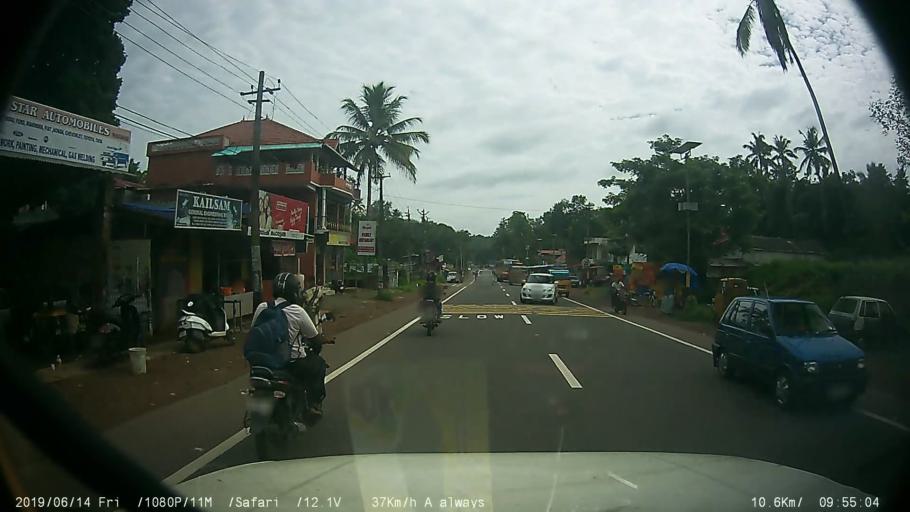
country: IN
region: Kerala
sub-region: Kottayam
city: Changanacheri
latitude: 9.5085
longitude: 76.5270
